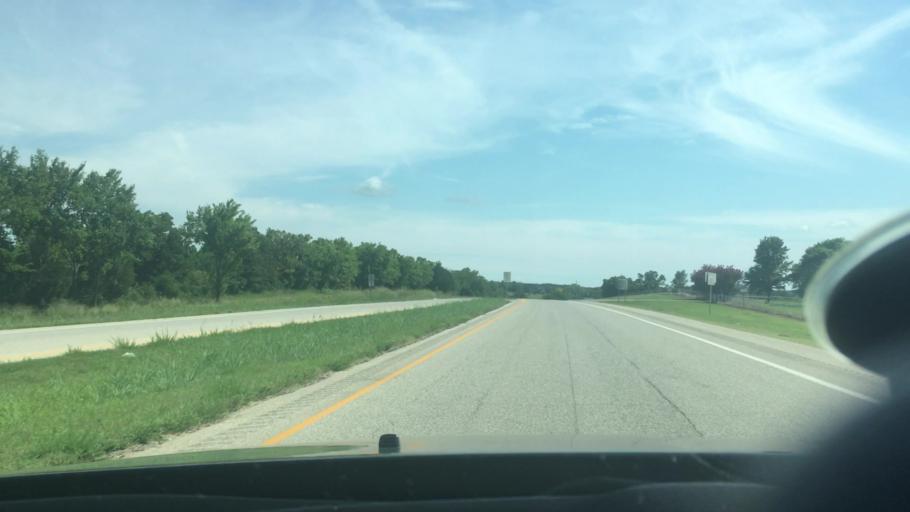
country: US
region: Oklahoma
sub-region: Seminole County
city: Seminole
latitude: 35.1845
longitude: -96.6752
